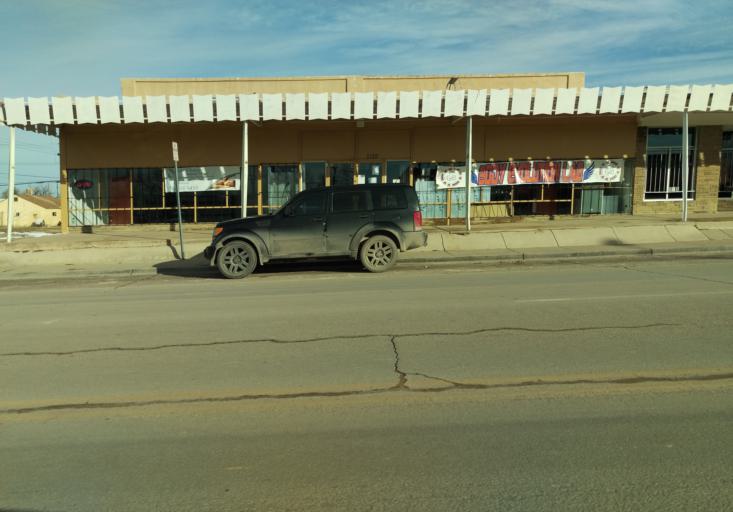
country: US
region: New Mexico
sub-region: Eddy County
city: Carlsbad
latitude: 32.4204
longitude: -104.2407
